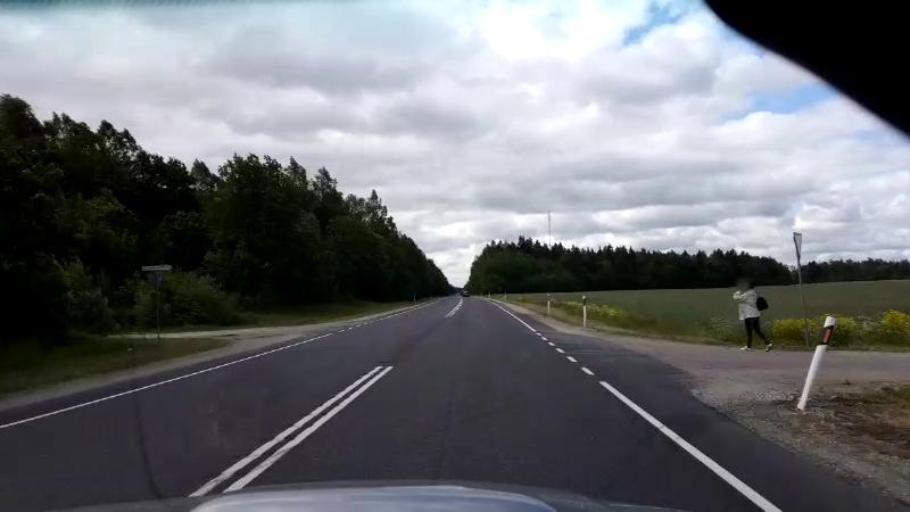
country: EE
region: Raplamaa
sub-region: Maerjamaa vald
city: Marjamaa
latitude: 58.9159
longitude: 24.4568
